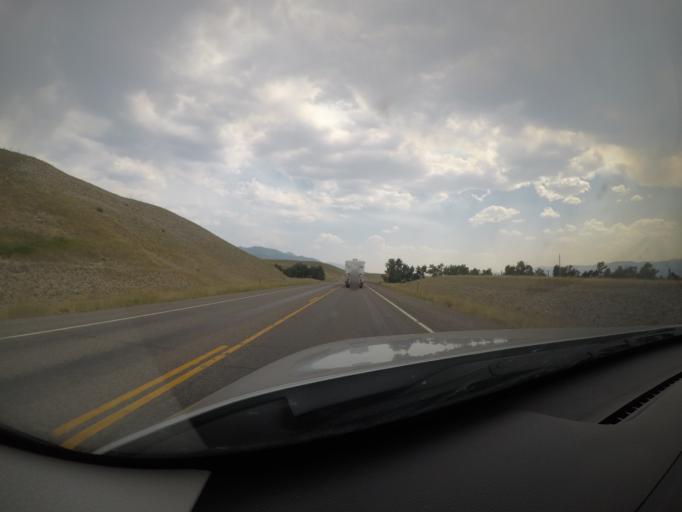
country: US
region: Montana
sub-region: Gallatin County
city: Big Sky
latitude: 45.1048
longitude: -111.6516
